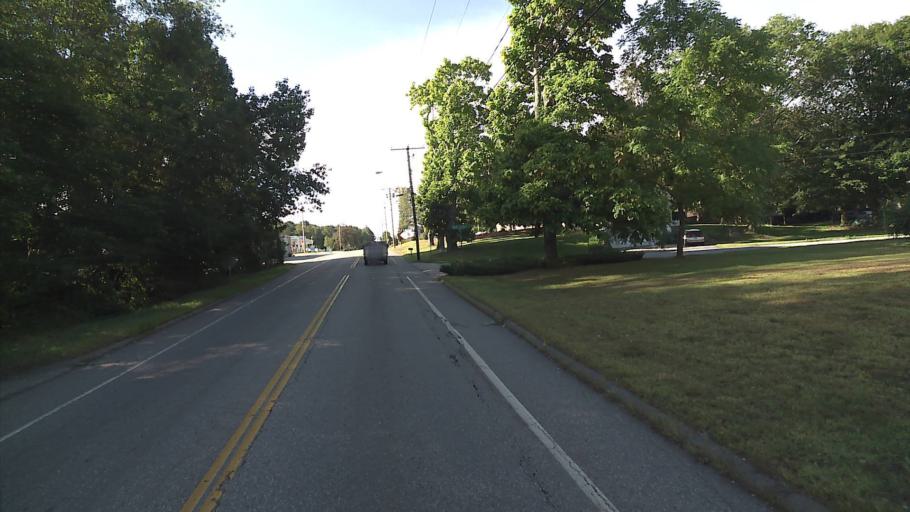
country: US
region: Connecticut
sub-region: New London County
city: Uncasville
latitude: 41.4262
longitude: -72.1102
